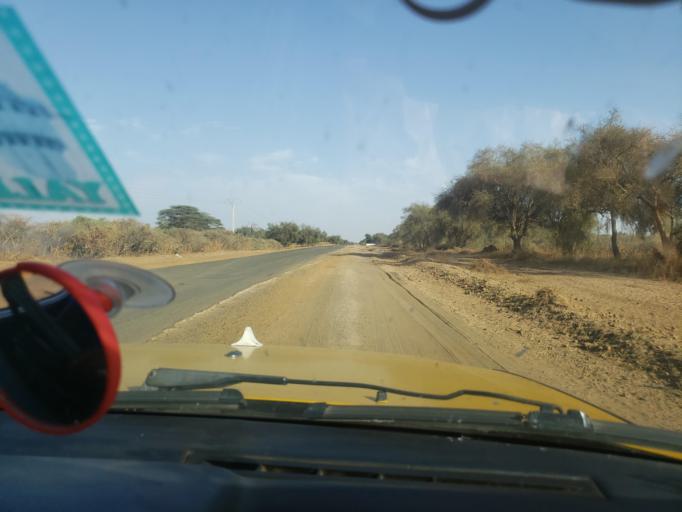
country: SN
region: Louga
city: Louga
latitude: 15.5035
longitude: -15.9503
